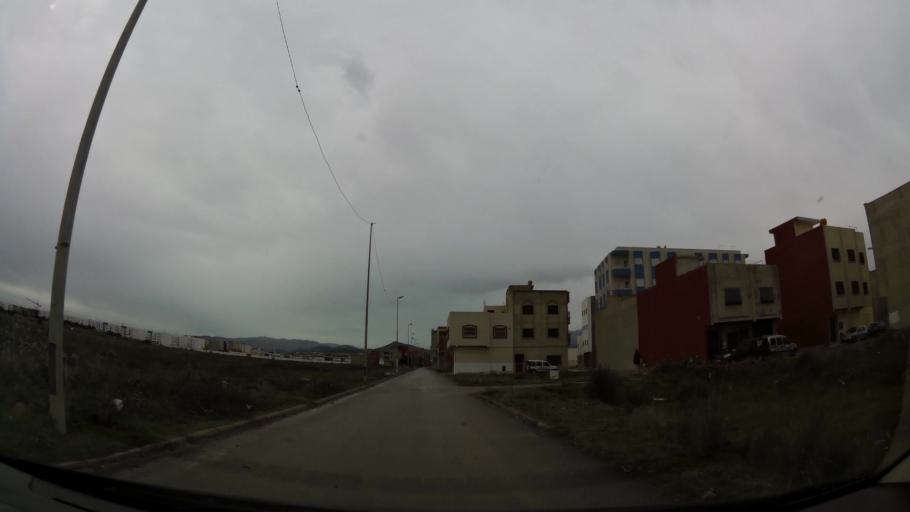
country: MA
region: Tanger-Tetouan
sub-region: Tetouan
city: Martil
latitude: 35.6175
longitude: -5.2984
